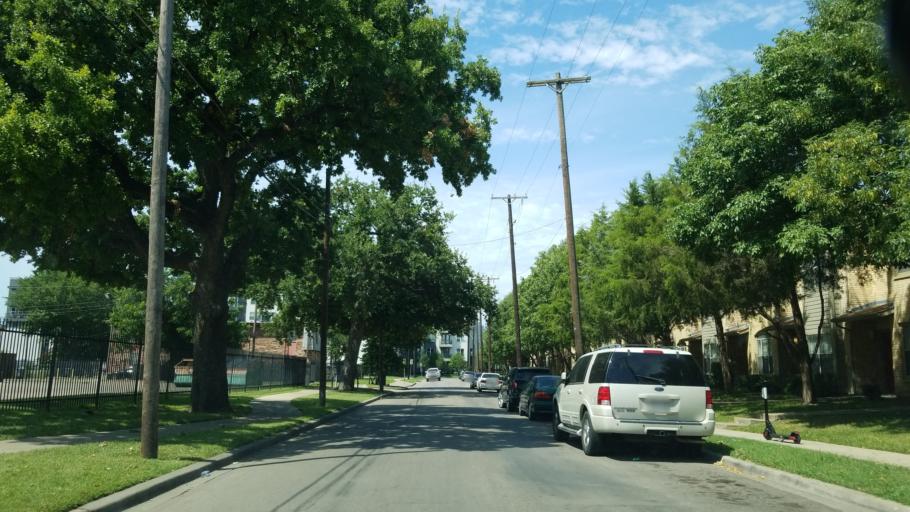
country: US
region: Texas
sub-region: Dallas County
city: Dallas
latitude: 32.7986
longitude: -96.7888
